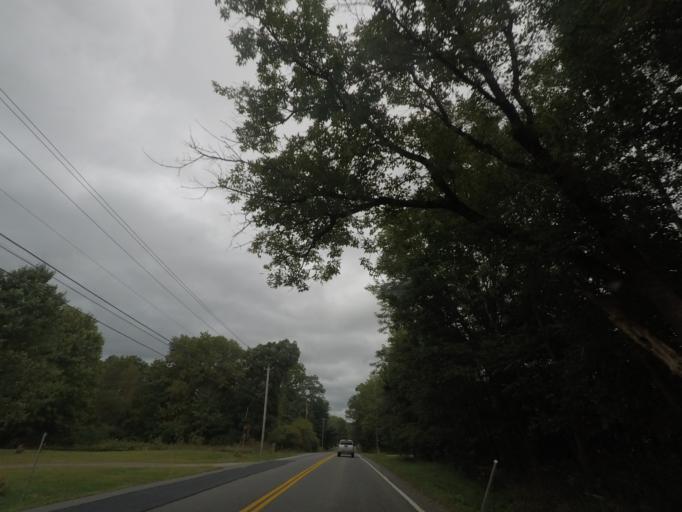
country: US
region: New York
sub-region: Washington County
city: Cambridge
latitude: 42.9471
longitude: -73.4443
